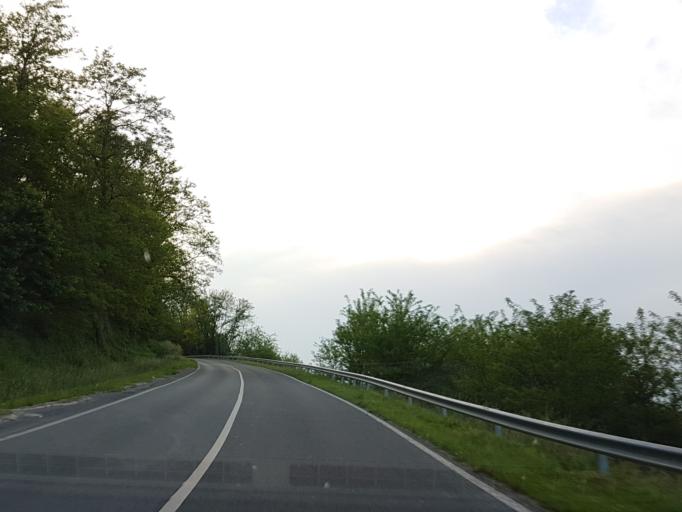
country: HU
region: Zala
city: Zalaegerszeg
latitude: 46.8601
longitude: 16.7769
